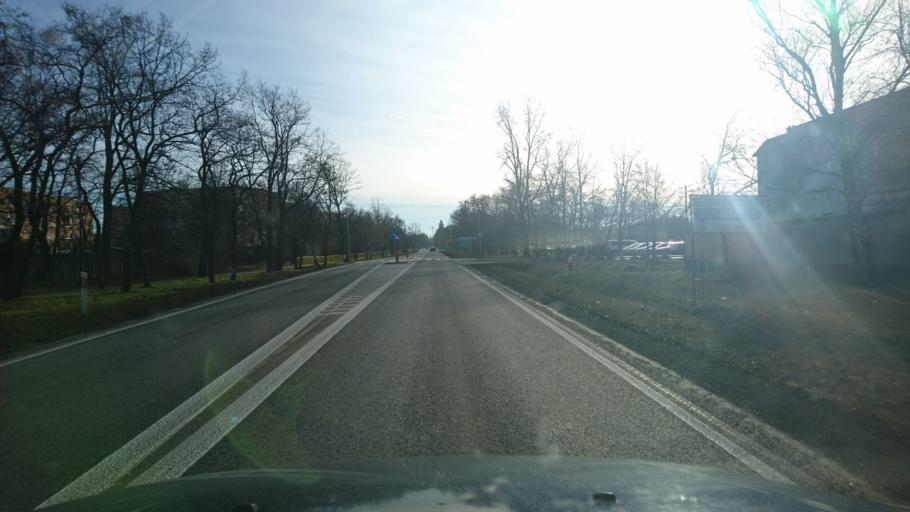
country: PL
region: Greater Poland Voivodeship
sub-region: Powiat ostrzeszowski
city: Ostrzeszow
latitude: 51.4318
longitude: 17.9181
